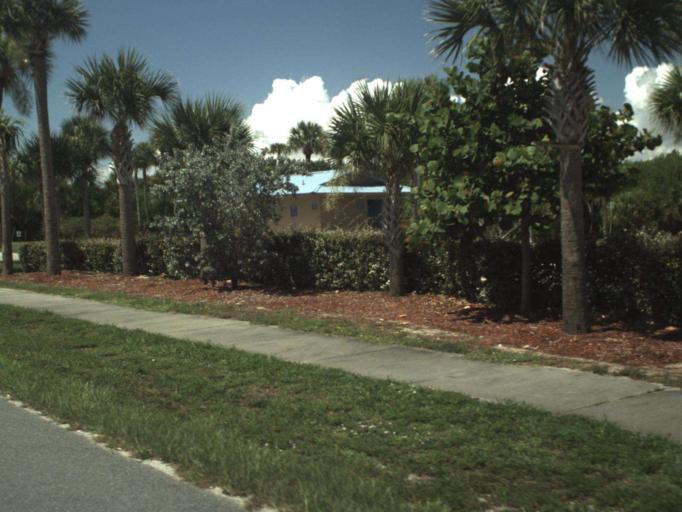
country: US
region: Florida
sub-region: Saint Lucie County
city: Fort Pierce
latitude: 27.4958
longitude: -80.3011
